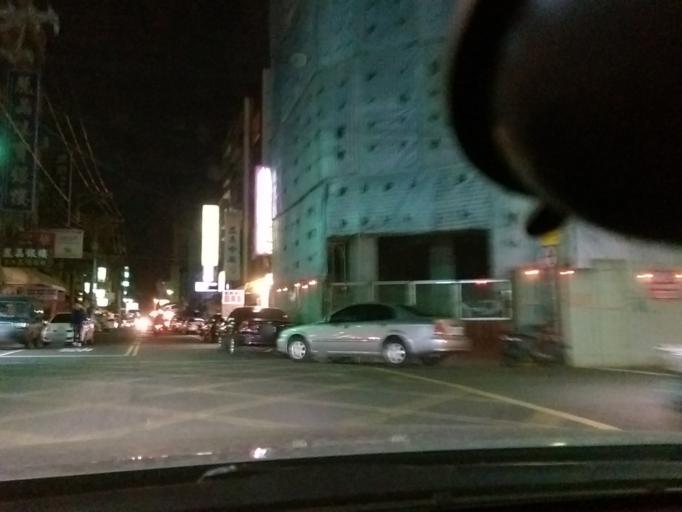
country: TW
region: Taiwan
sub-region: Chiayi
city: Jiayi Shi
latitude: 23.4800
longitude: 120.4541
